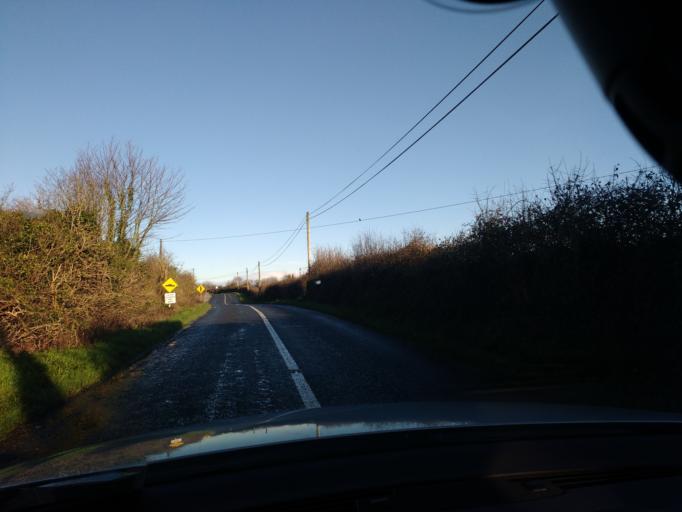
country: IE
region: Leinster
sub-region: Laois
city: Rathdowney
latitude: 52.6830
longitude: -7.5950
